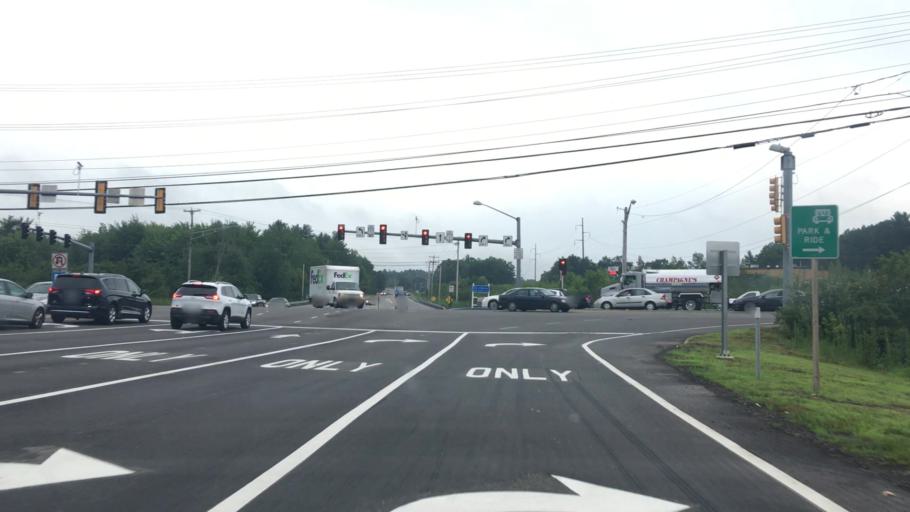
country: US
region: Maine
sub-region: York County
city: Biddeford
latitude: 43.4784
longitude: -70.4968
